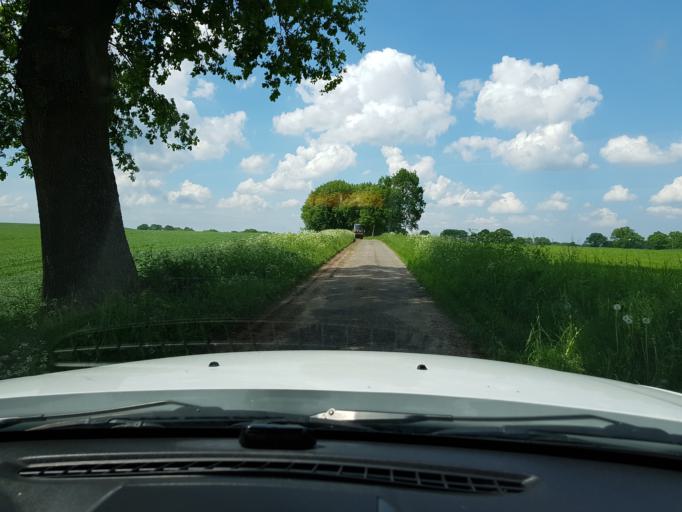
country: PL
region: West Pomeranian Voivodeship
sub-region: Powiat drawski
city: Drawsko Pomorskie
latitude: 53.5289
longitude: 15.7458
